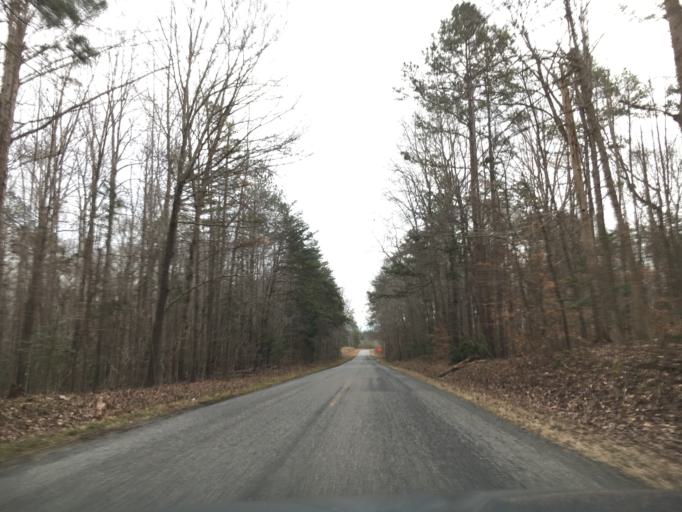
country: US
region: Virginia
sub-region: Amelia County
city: Amelia Court House
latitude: 37.4250
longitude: -77.9983
